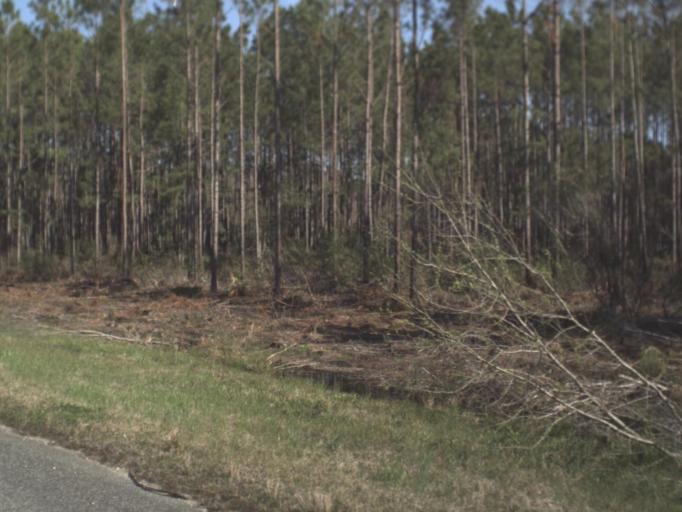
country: US
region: Florida
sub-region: Leon County
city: Woodville
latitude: 30.2873
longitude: -84.0444
